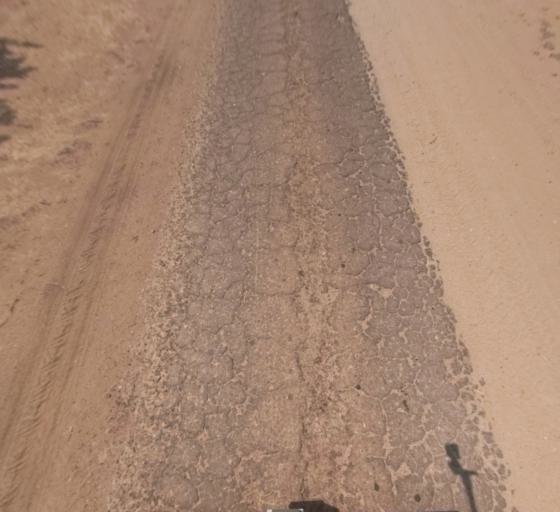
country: US
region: California
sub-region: Madera County
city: Fairmead
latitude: 37.1450
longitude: -120.1292
